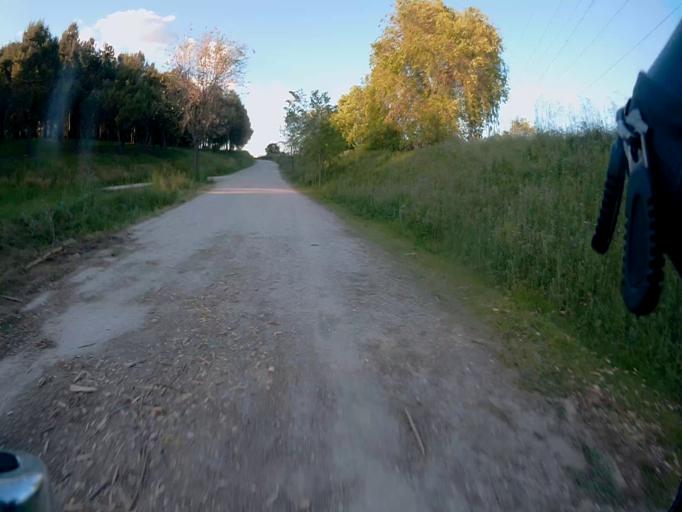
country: ES
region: Madrid
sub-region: Provincia de Madrid
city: Leganes
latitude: 40.3220
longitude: -3.7889
